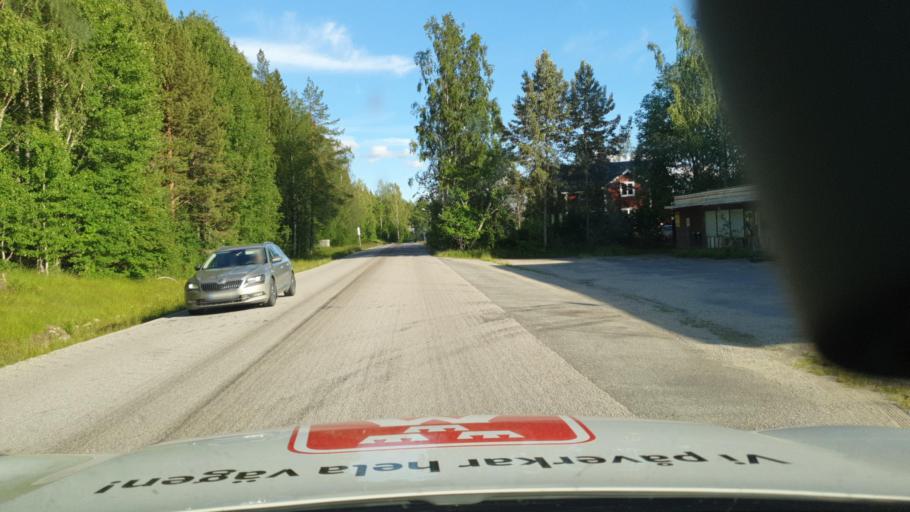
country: SE
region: Vaesterbotten
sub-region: Vindelns Kommun
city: Vindeln
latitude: 64.1538
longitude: 19.5096
